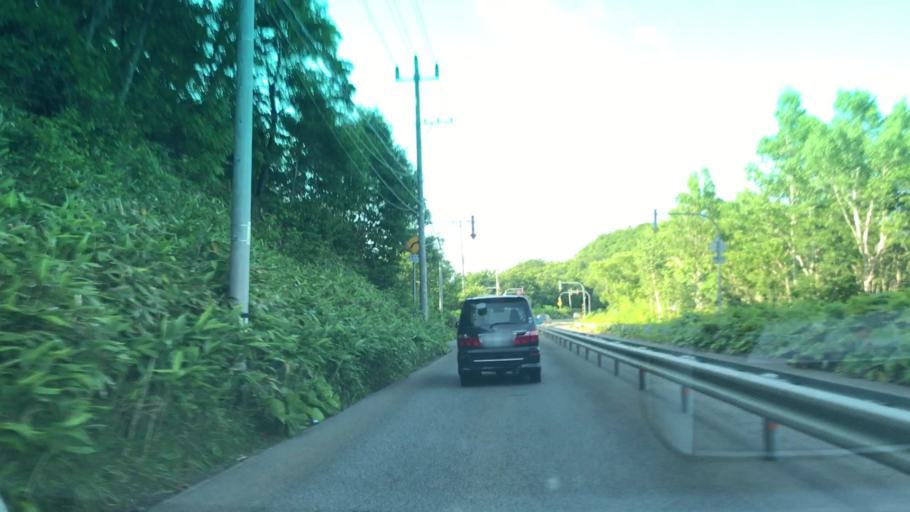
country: JP
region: Hokkaido
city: Otaru
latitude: 43.1436
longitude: 141.0118
